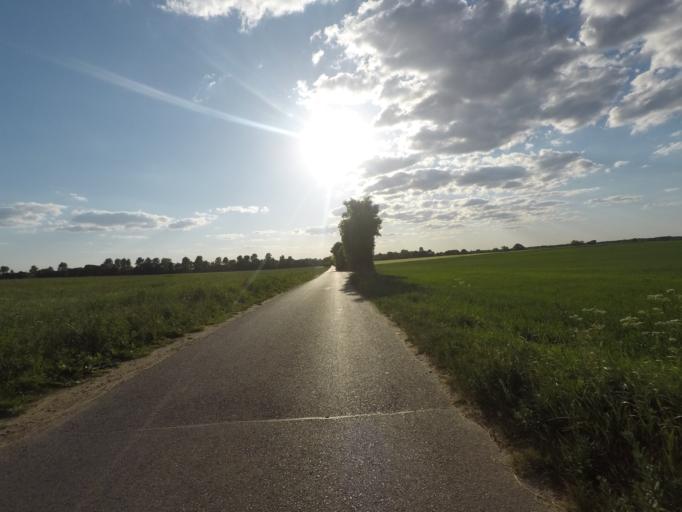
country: DE
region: Brandenburg
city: Britz
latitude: 52.8788
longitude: 13.7523
